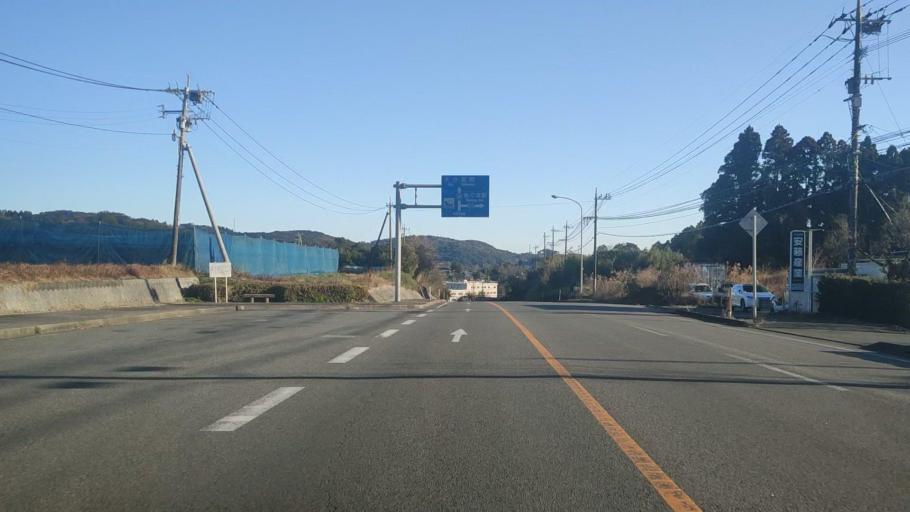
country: JP
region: Miyazaki
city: Takanabe
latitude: 32.3268
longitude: 131.6006
